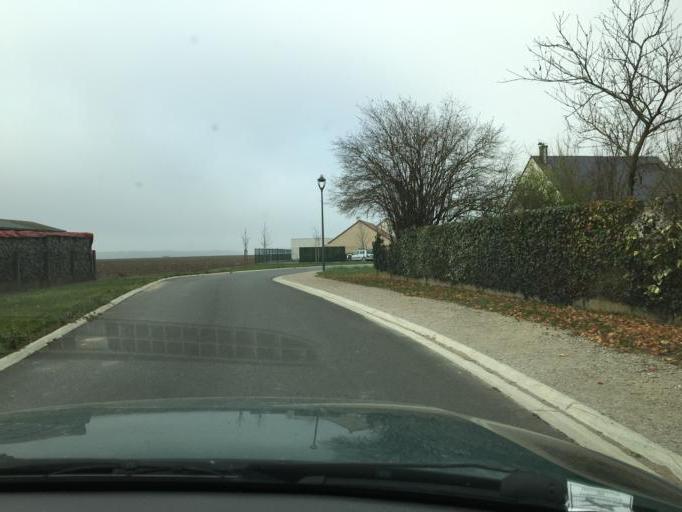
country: FR
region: Centre
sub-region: Departement du Loiret
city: Gidy
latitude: 47.9817
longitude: 1.8399
